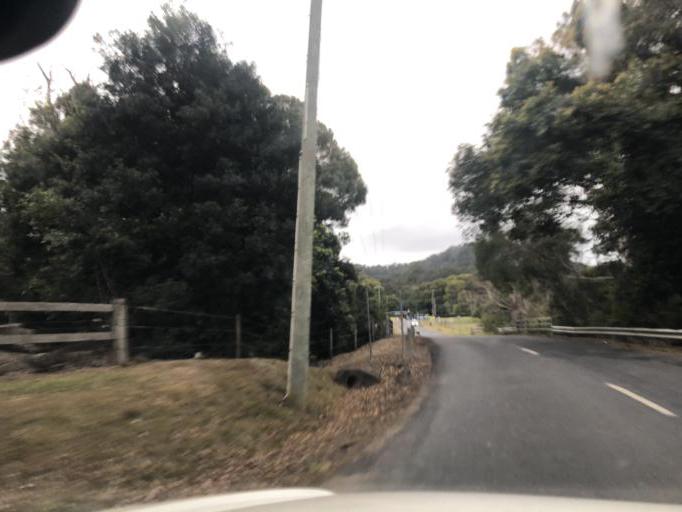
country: AU
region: New South Wales
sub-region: Coffs Harbour
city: Coffs Harbour
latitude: -30.2558
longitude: 153.0457
